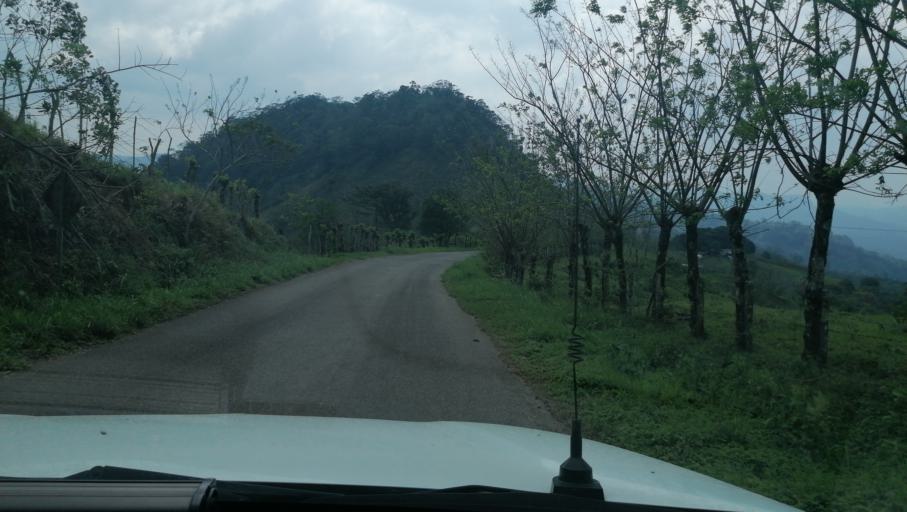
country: MX
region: Chiapas
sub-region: Francisco Leon
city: San Miguel la Sardina
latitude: 17.2379
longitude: -93.3194
